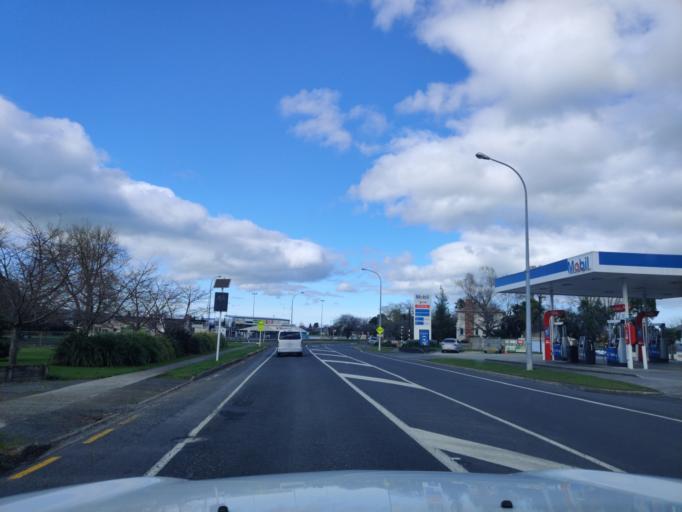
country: NZ
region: Waikato
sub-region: Matamata-Piako District
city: Matamata
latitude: -37.8139
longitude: 175.7707
